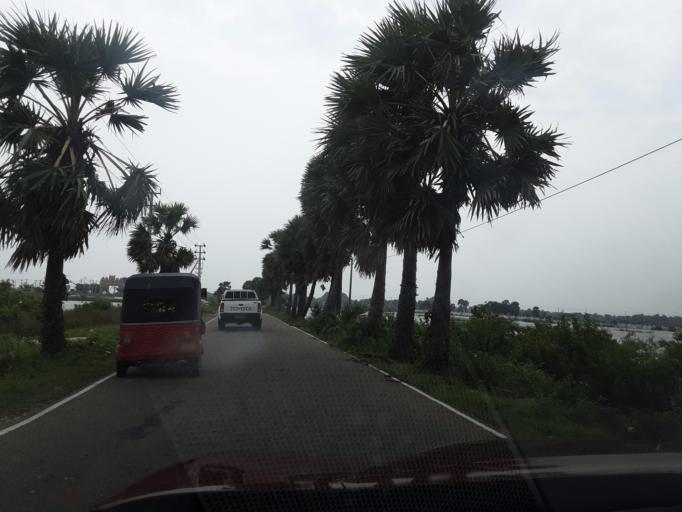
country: LK
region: Northern Province
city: Jaffna
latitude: 9.6652
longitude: 80.0588
